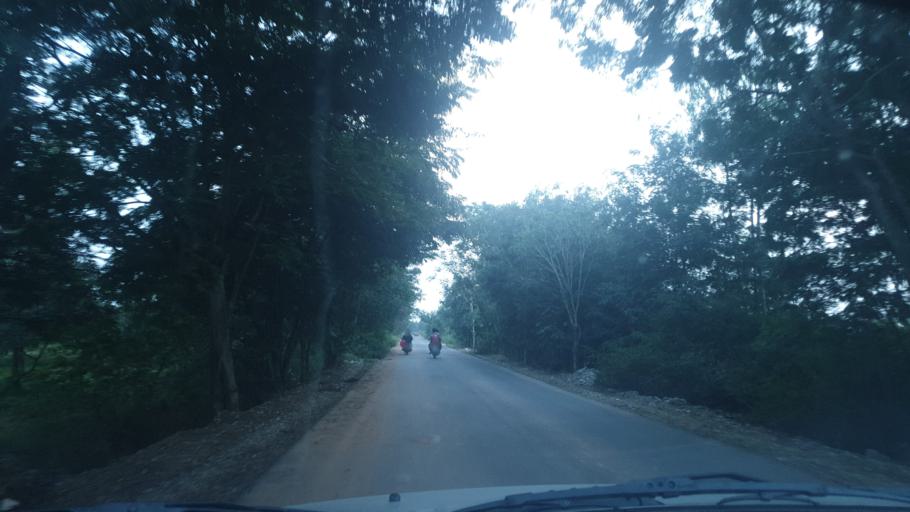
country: IN
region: Karnataka
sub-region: Bangalore Rural
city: Hoskote
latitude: 13.0831
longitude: 77.7025
